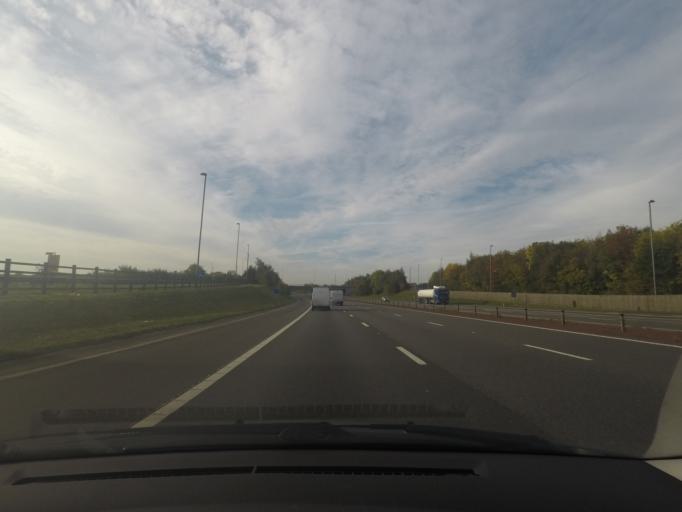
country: GB
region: England
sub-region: City and Borough of Leeds
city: Swillington
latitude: 53.7947
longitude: -1.4242
